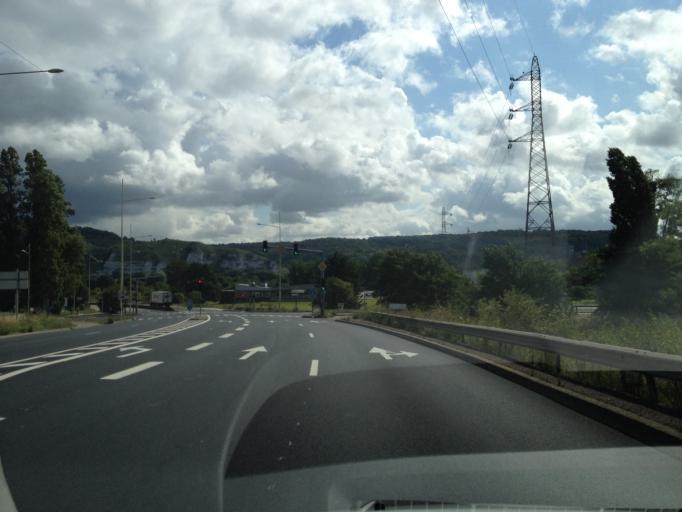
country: FR
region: Haute-Normandie
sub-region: Departement de la Seine-Maritime
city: Saint-Etienne-du-Rouvray
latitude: 49.3676
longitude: 1.1096
